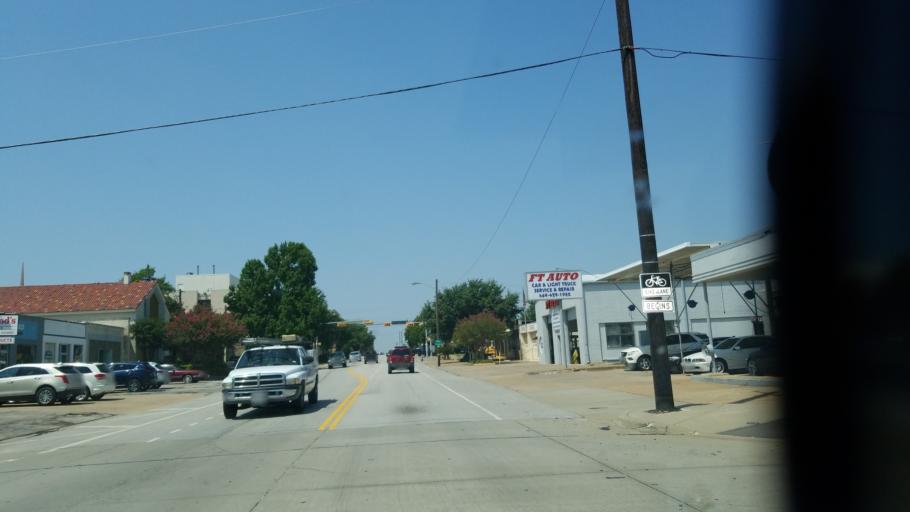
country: US
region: Texas
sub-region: Dallas County
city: Garland
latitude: 32.9127
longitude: -96.6390
